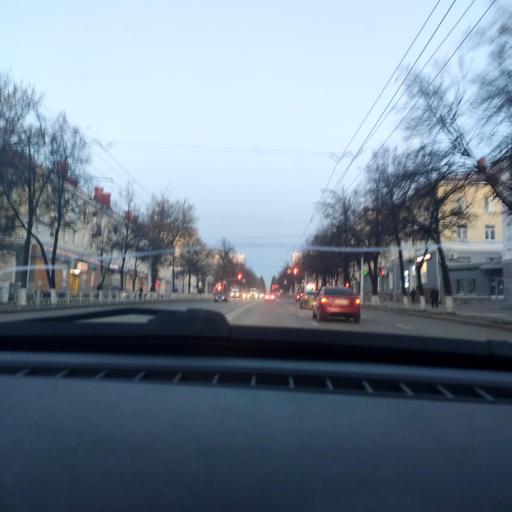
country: RU
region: Bashkortostan
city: Ufa
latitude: 54.8158
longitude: 56.0814
